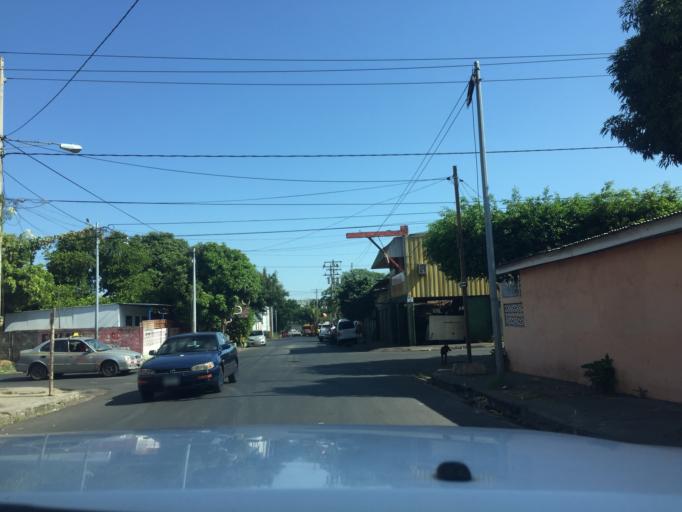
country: NI
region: Managua
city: Managua
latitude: 12.1514
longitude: -86.2549
